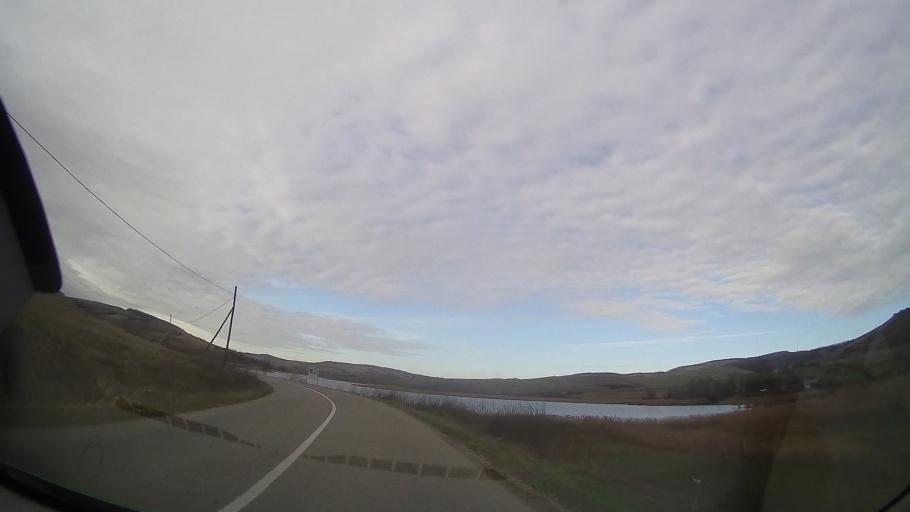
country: RO
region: Cluj
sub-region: Comuna Geaca
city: Geaca
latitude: 46.8444
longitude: 24.1213
